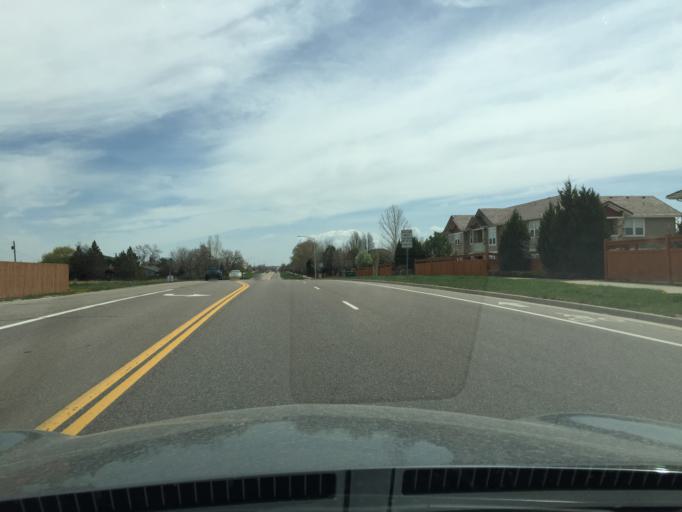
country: US
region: Colorado
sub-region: Broomfield County
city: Broomfield
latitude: 39.9578
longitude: -105.0315
